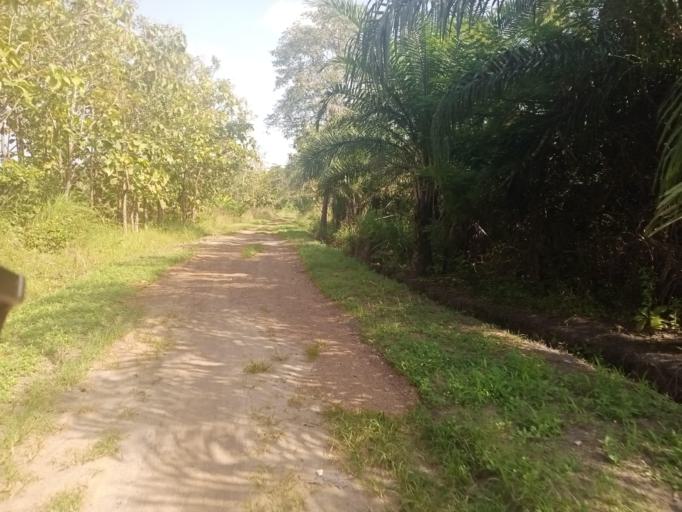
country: TG
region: Maritime
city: Tsevie
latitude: 6.6601
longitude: 0.9720
